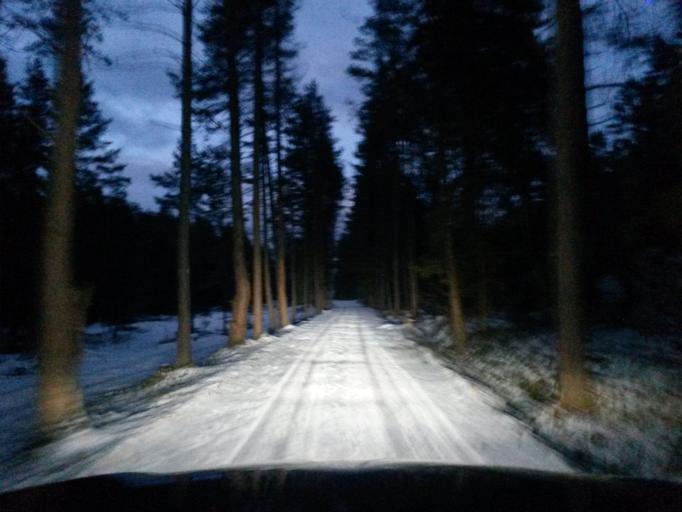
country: SK
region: Kosicky
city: Medzev
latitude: 48.7916
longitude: 20.8064
